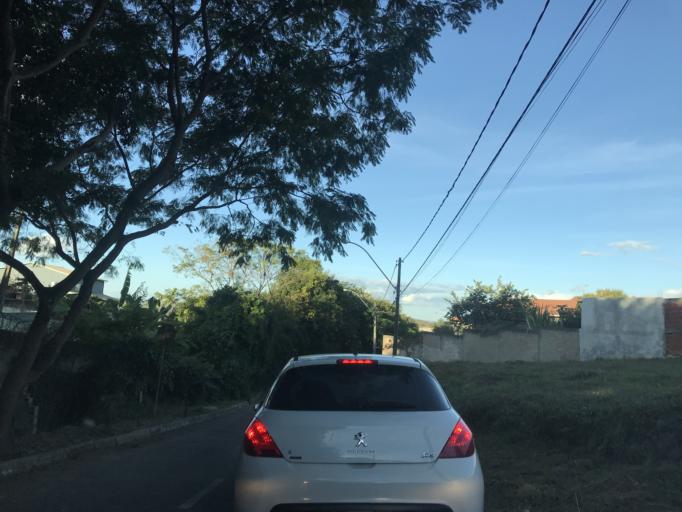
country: BR
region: Federal District
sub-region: Brasilia
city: Brasilia
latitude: -15.8812
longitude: -47.7662
